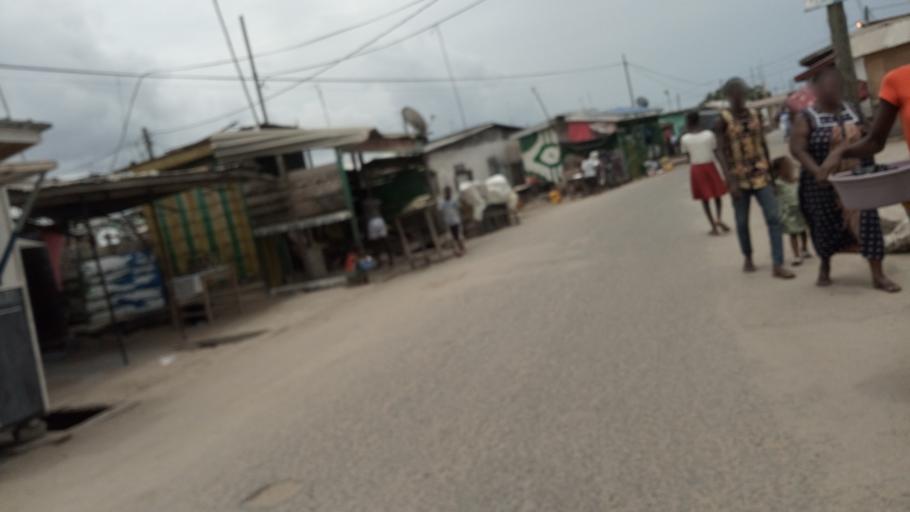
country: GH
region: Central
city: Winneba
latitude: 5.3408
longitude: -0.6201
